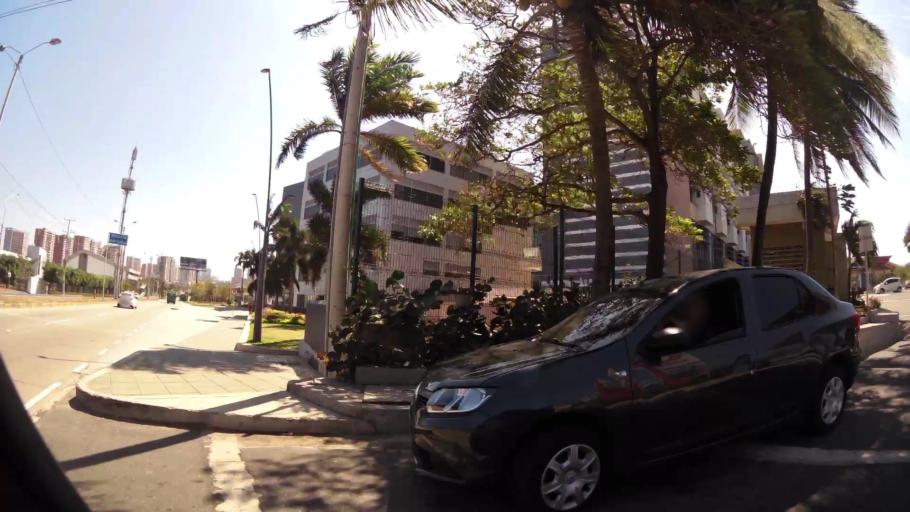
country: CO
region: Atlantico
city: Barranquilla
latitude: 11.0164
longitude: -74.8468
